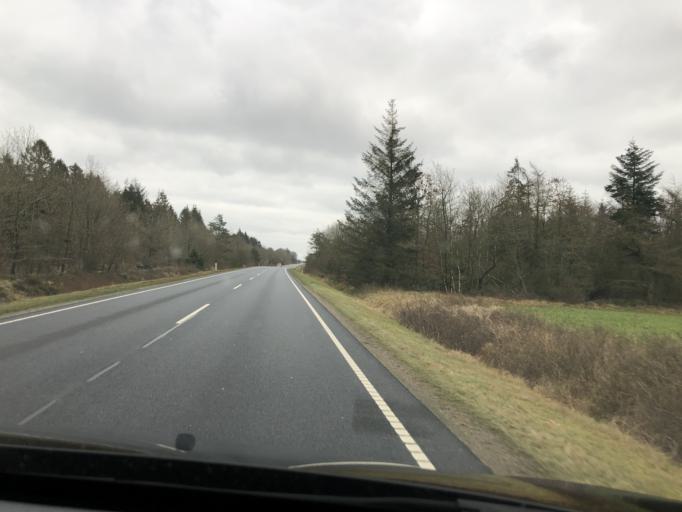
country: DK
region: South Denmark
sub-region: Billund Kommune
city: Grindsted
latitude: 55.8468
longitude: 8.8431
